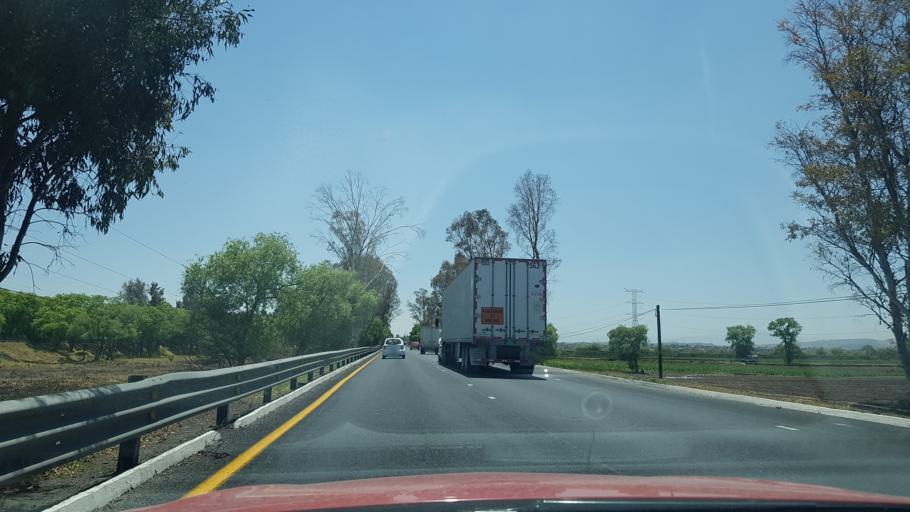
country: MX
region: Mexico
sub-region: Ixtlahuaca
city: San Francisco de Guzman
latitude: 19.6146
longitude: -99.7766
